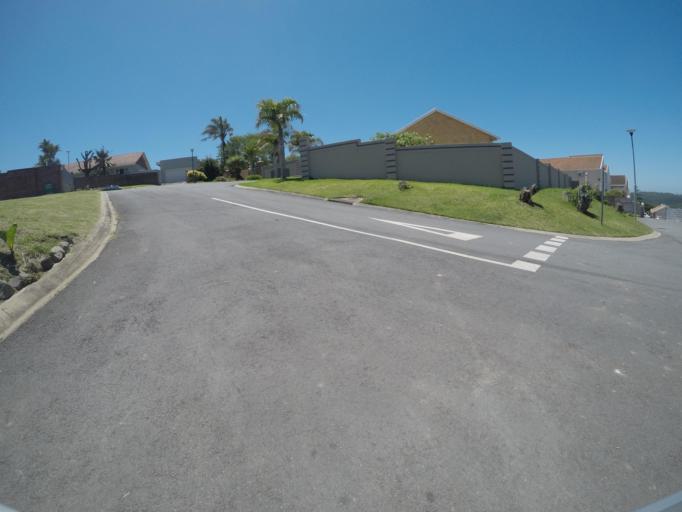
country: ZA
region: Eastern Cape
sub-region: Buffalo City Metropolitan Municipality
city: East London
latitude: -32.9541
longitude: 27.9379
